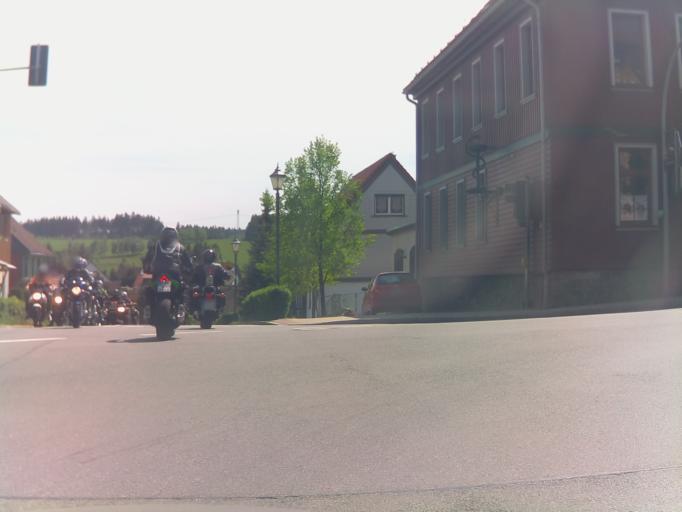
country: DE
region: Saxony-Anhalt
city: Hasselfelde
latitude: 51.6902
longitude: 10.8563
